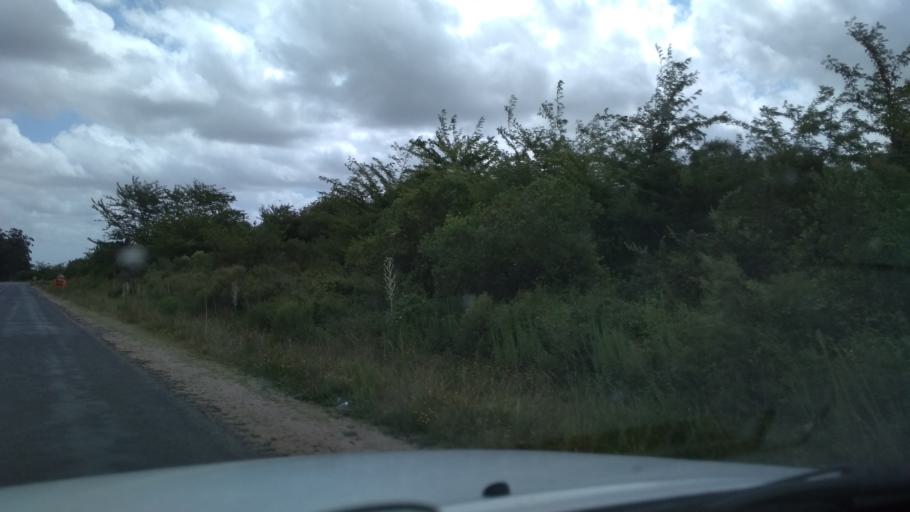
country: UY
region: Canelones
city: San Ramon
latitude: -34.2726
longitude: -55.9460
